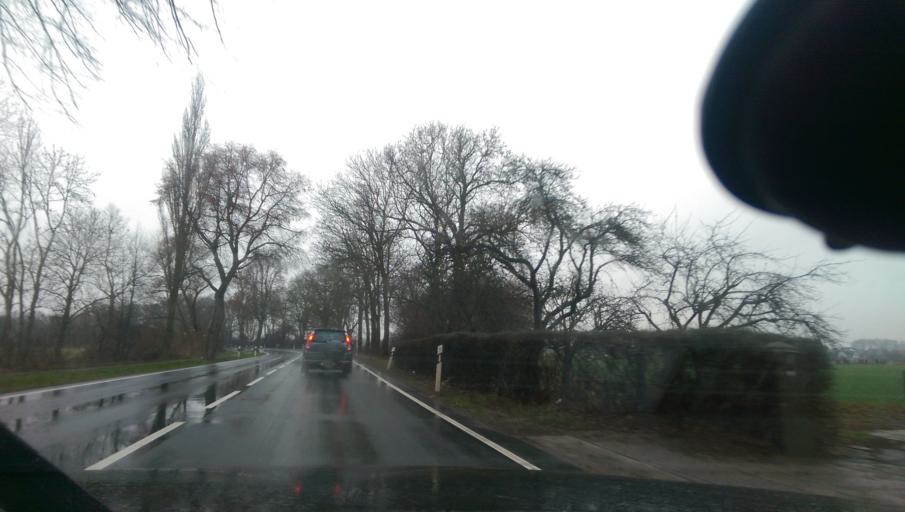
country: DE
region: Lower Saxony
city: Verden
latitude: 52.8926
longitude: 9.2202
